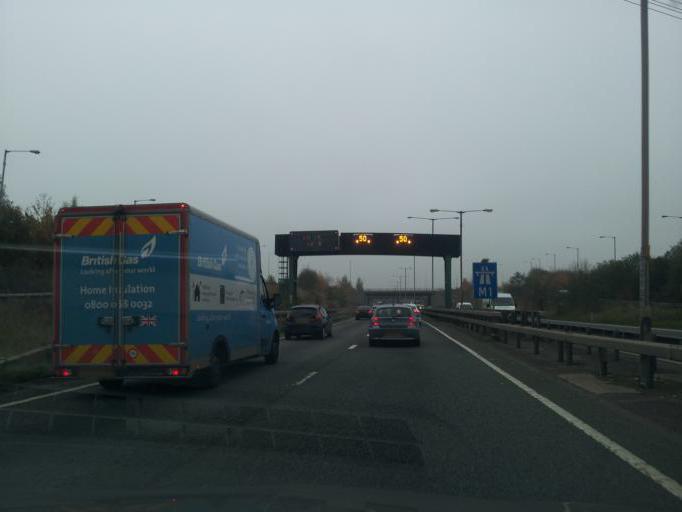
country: GB
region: England
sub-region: Leicestershire
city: Kirby Muxloe
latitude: 52.6463
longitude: -1.2228
